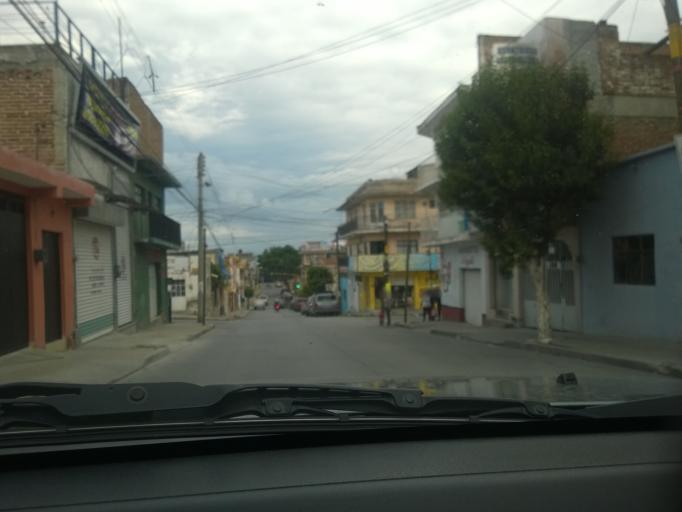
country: MX
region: Guanajuato
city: Leon
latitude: 21.1317
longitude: -101.6928
